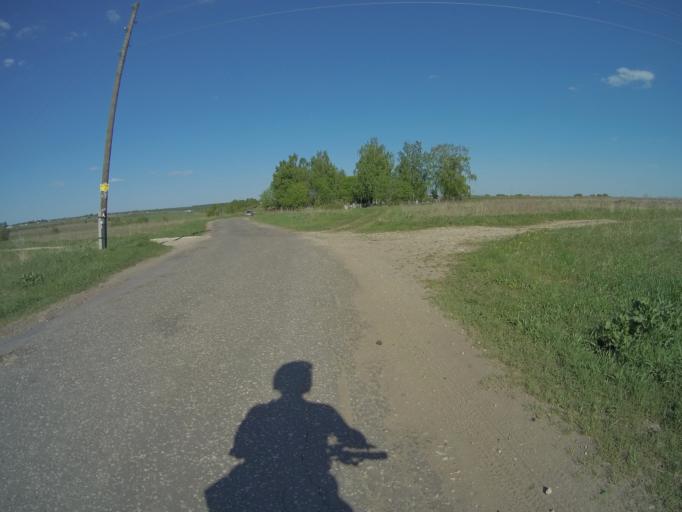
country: RU
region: Vladimir
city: Kideksha
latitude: 56.4113
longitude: 40.5023
